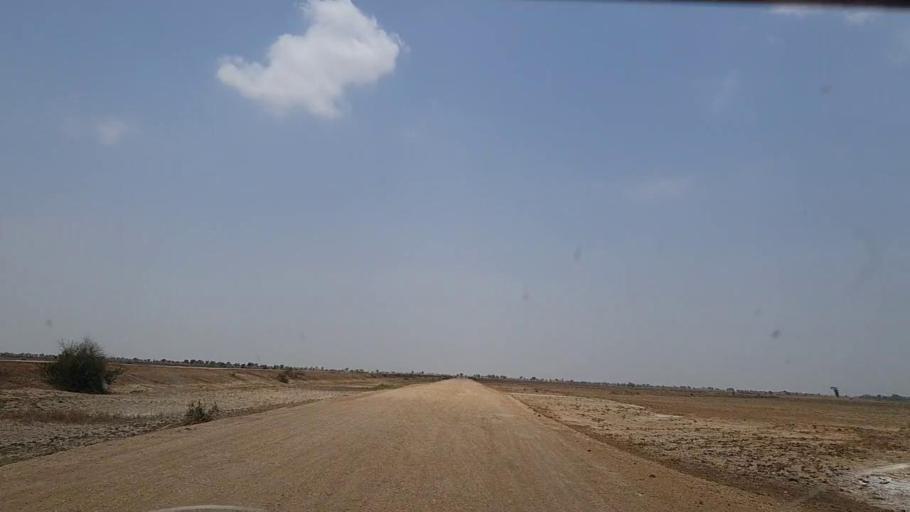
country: PK
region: Sindh
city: Phulji
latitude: 26.7916
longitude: 67.6423
